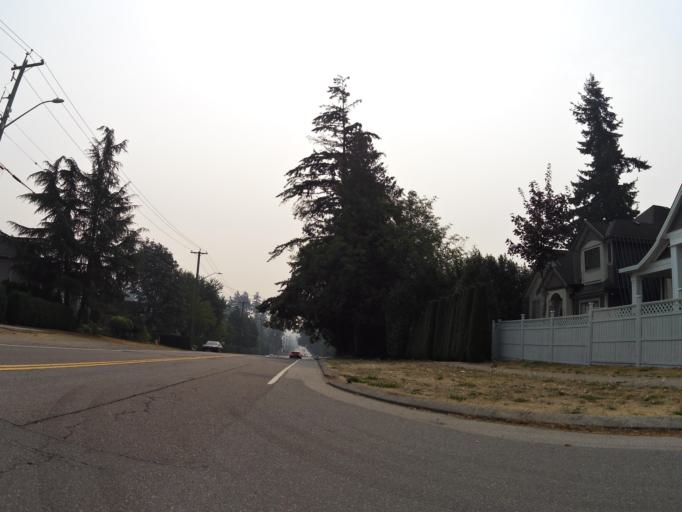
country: CA
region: British Columbia
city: Surrey
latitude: 49.1095
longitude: -122.7567
